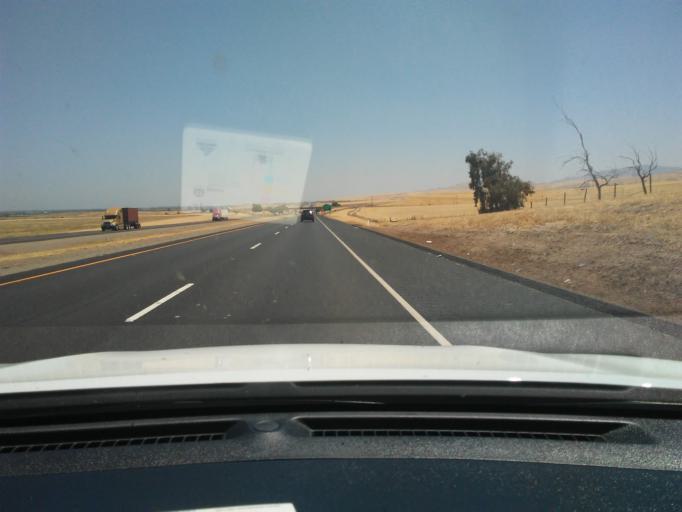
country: US
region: California
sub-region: San Joaquin County
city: Tracy
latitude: 37.6758
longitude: -121.4637
